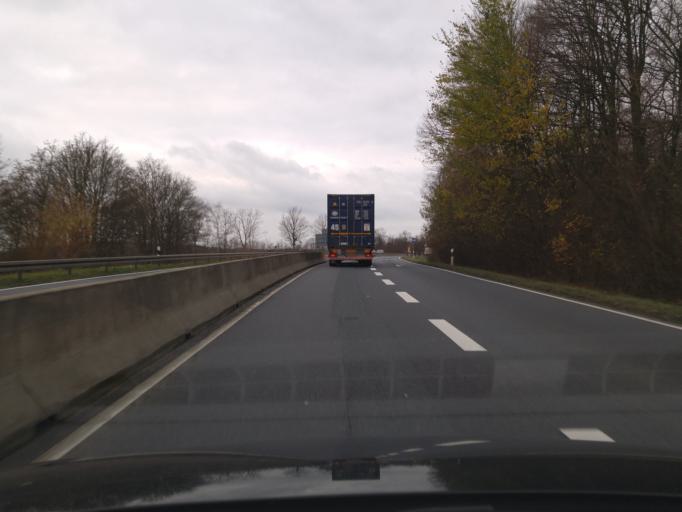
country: DE
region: Lower Saxony
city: Holle
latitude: 52.1047
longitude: 10.1508
